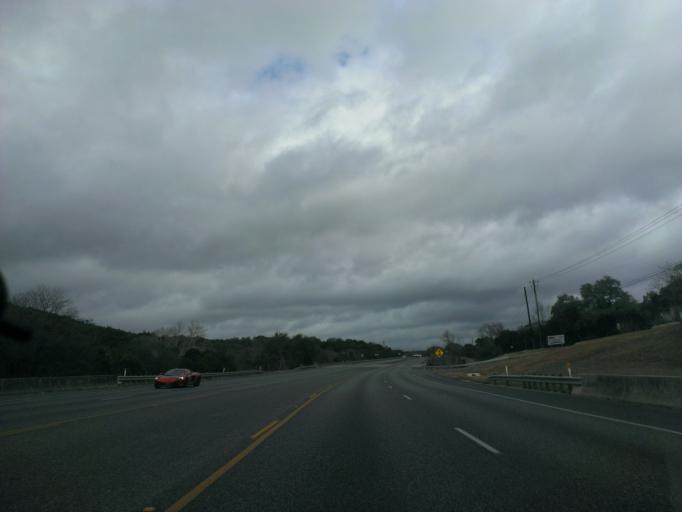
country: US
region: Texas
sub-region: Travis County
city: West Lake Hills
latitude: 30.3620
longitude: -97.7947
